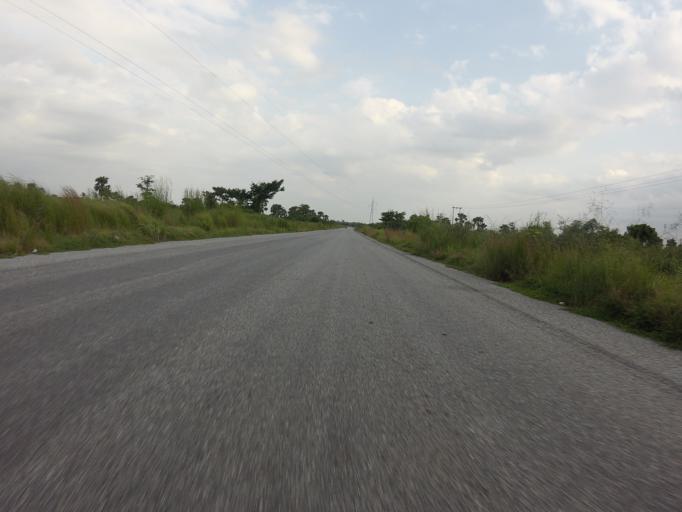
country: GH
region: Volta
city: Ho
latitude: 6.3910
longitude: 0.5266
